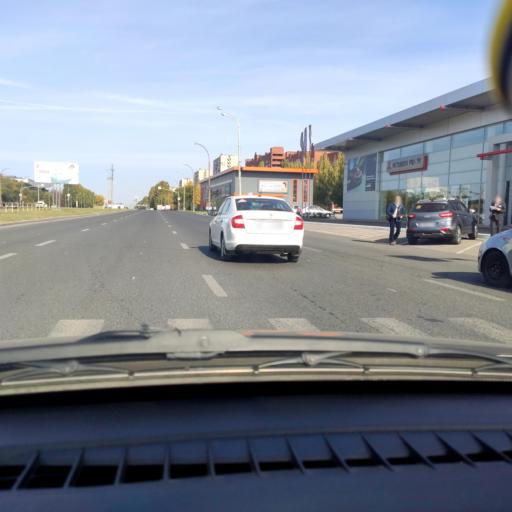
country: RU
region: Samara
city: Tol'yatti
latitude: 53.5007
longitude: 49.2749
